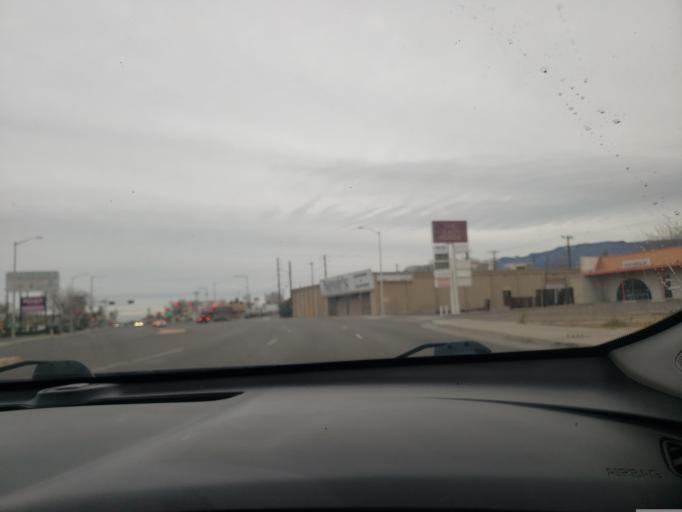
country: US
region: New Mexico
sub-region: Bernalillo County
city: Albuquerque
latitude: 35.1077
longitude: -106.5865
